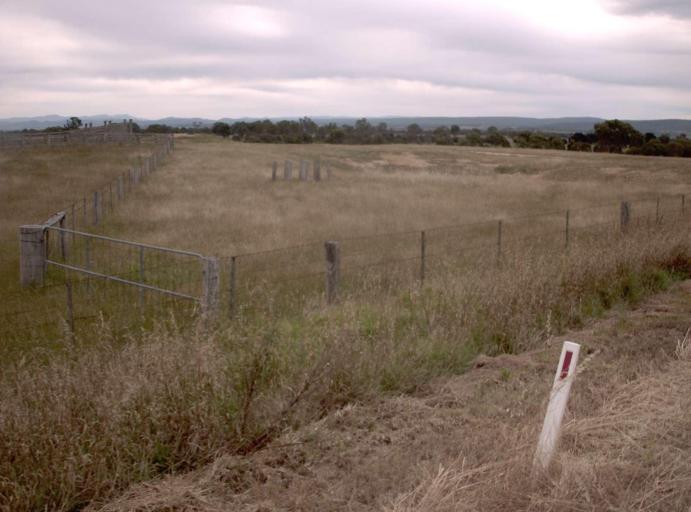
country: AU
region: Victoria
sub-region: East Gippsland
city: Bairnsdale
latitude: -37.8733
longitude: 147.5605
